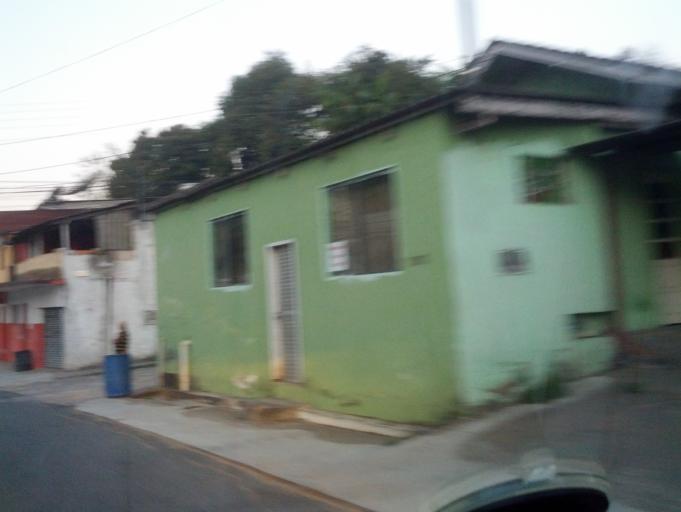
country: BR
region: Santa Catarina
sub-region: Blumenau
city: Blumenau
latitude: -26.9100
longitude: -49.1084
